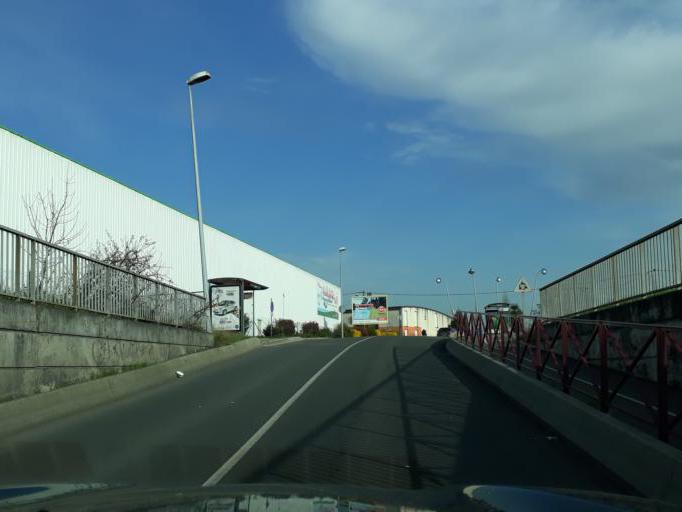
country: FR
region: Centre
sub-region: Departement du Loiret
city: La Chapelle-Saint-Mesmin
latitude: 47.8970
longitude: 1.8367
